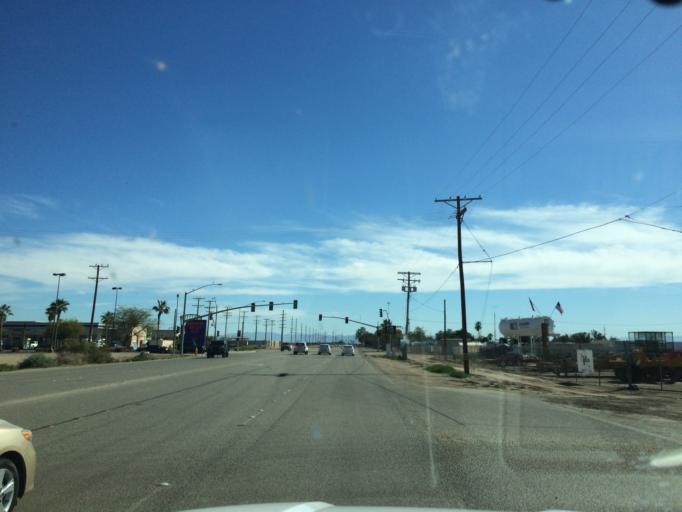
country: US
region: California
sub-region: Imperial County
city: Heber
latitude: 32.7623
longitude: -115.5351
